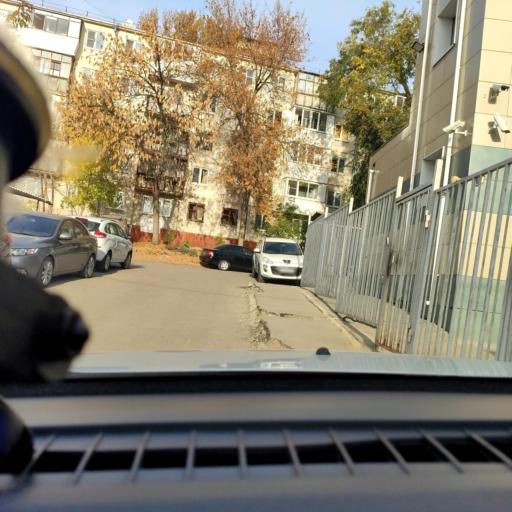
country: RU
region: Samara
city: Samara
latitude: 53.1898
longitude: 50.2092
